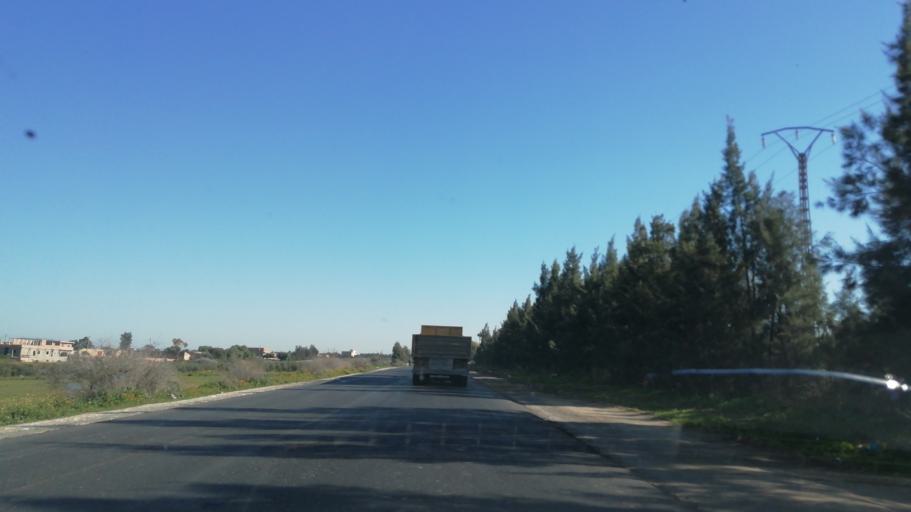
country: DZ
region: Relizane
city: Zemoura
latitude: 35.7575
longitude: 0.6695
